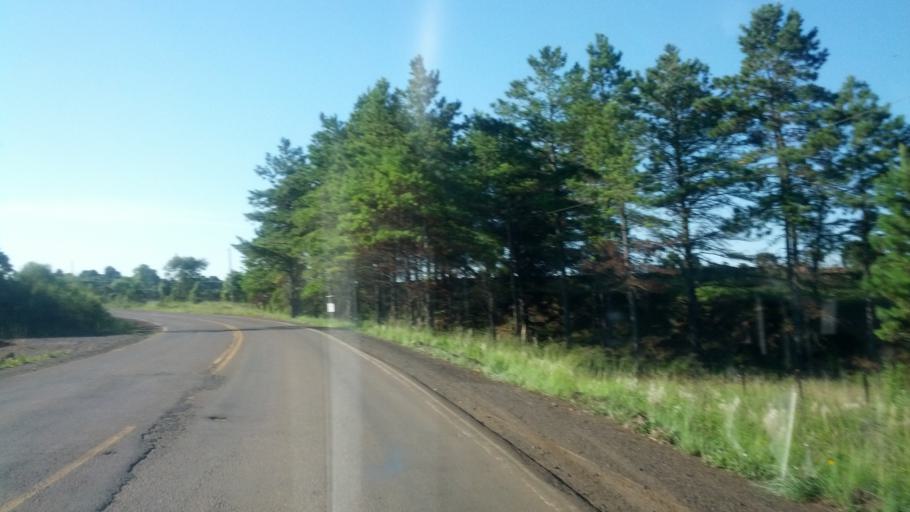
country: BR
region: Santa Catarina
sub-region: Lages
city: Lages
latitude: -27.9514
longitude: -50.4947
